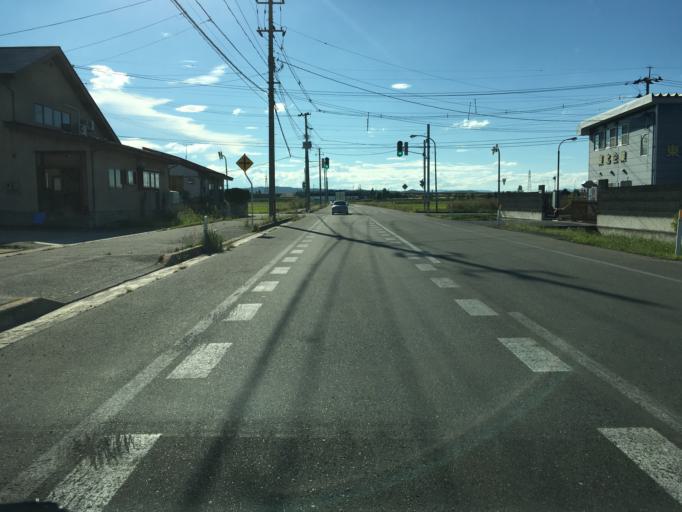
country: JP
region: Yamagata
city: Yonezawa
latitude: 37.9505
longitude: 140.1209
